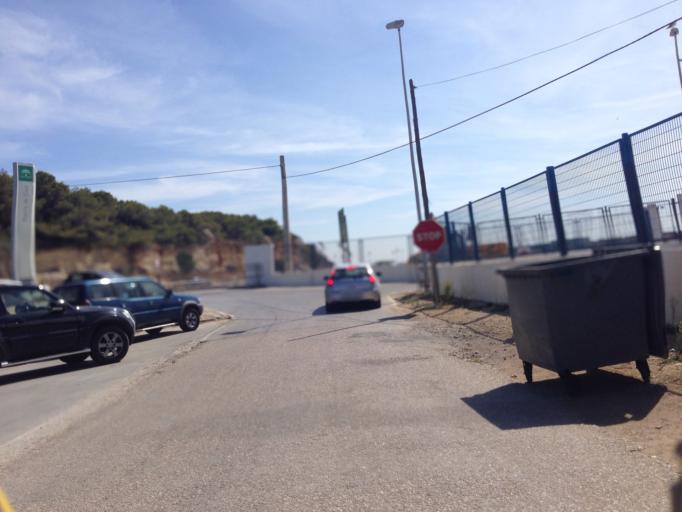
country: ES
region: Andalusia
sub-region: Provincia de Cadiz
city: Conil de la Frontera
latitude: 36.2971
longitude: -6.1382
